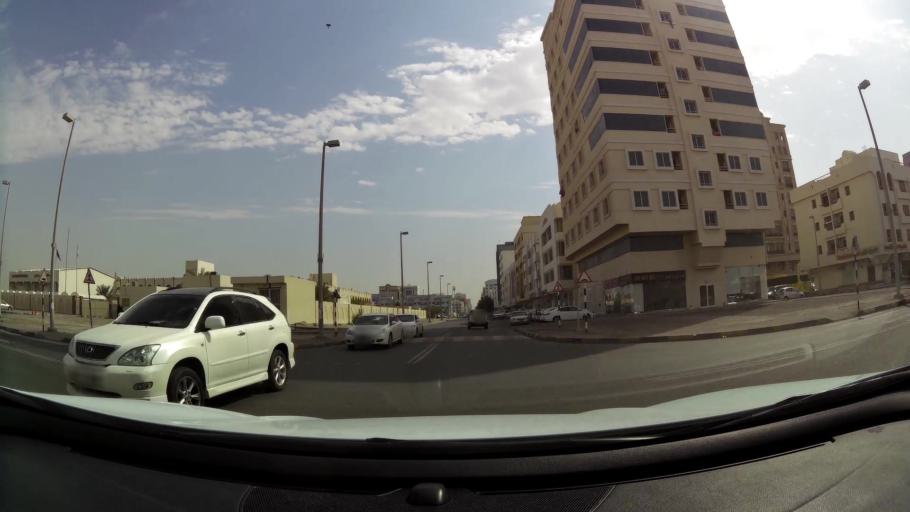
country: AE
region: Abu Dhabi
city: Abu Dhabi
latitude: 24.3337
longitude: 54.5366
